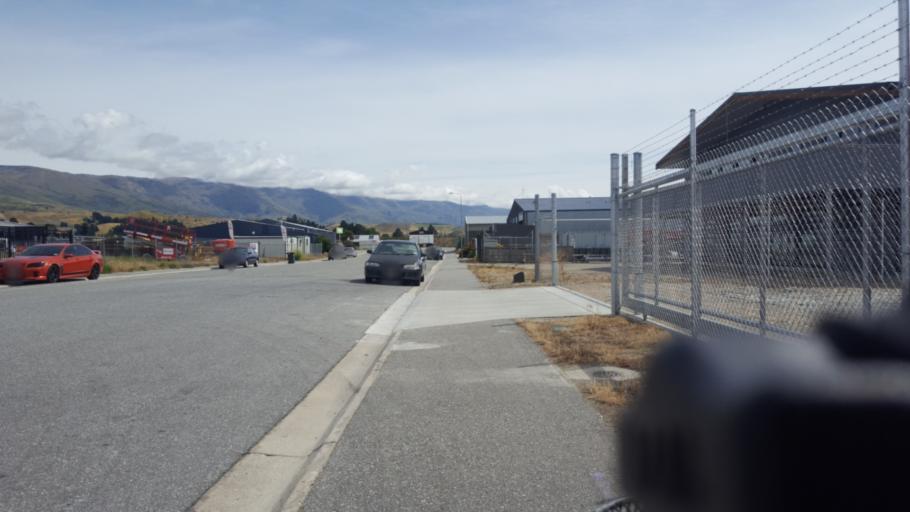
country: NZ
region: Otago
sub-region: Queenstown-Lakes District
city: Wanaka
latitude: -45.0512
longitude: 169.1916
